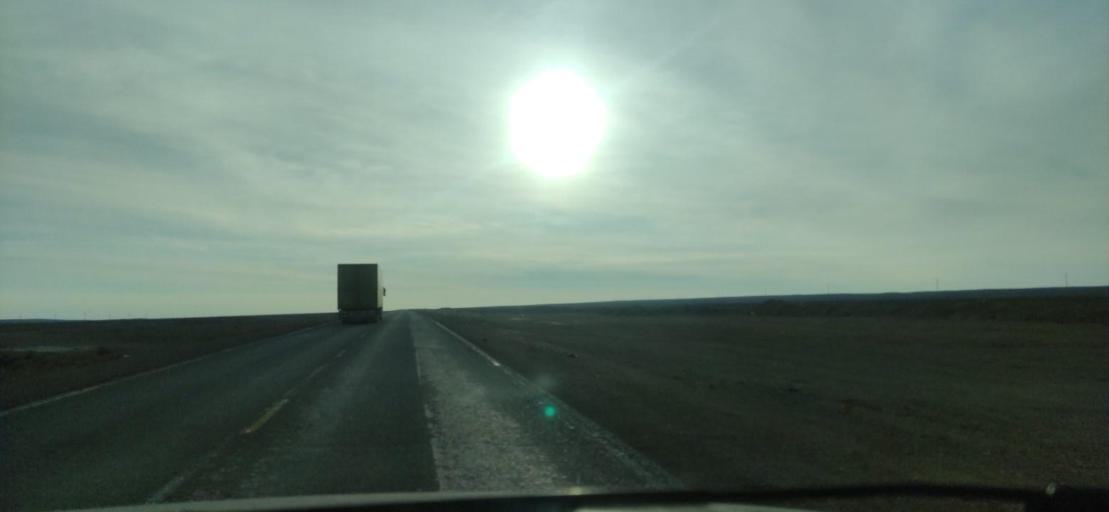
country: KZ
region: Qaraghandy
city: Saryshaghan
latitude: 46.2232
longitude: 73.6544
